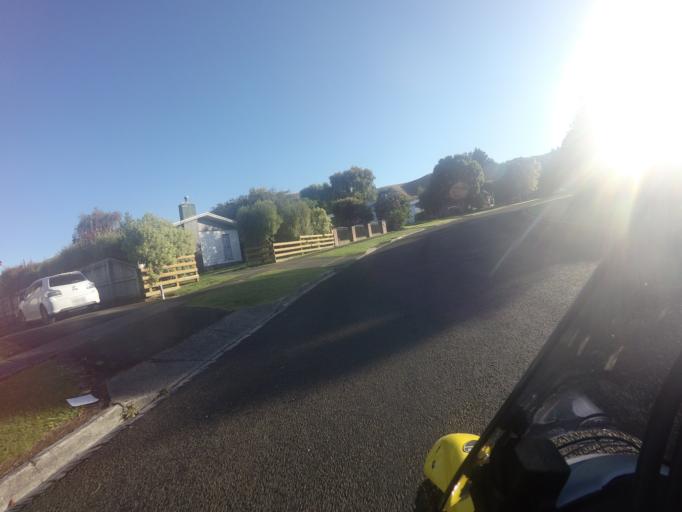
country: NZ
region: Gisborne
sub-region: Gisborne District
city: Gisborne
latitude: -38.6725
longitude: 178.0601
